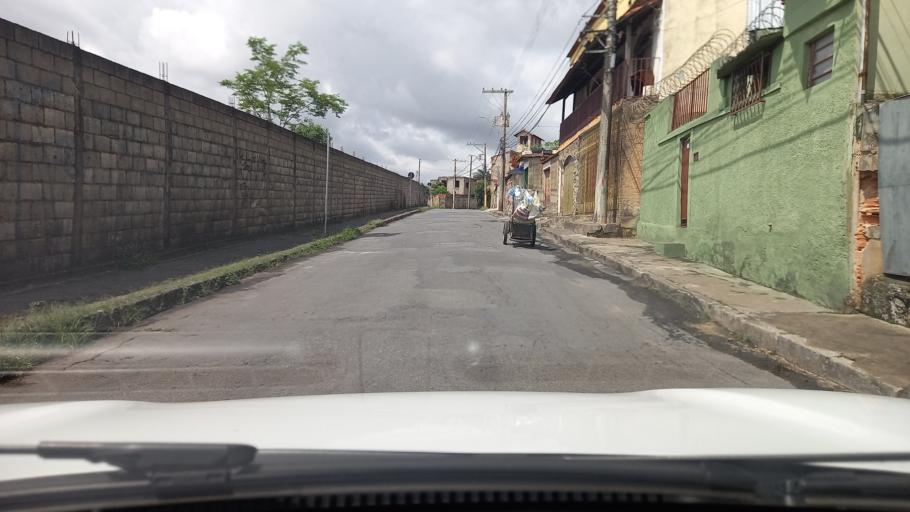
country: BR
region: Minas Gerais
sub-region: Contagem
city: Contagem
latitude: -19.8990
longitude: -44.0242
